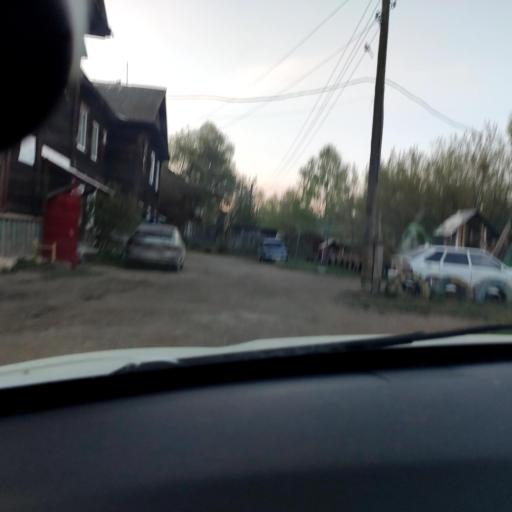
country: RU
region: Perm
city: Krasnokamsk
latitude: 58.0596
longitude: 55.8029
